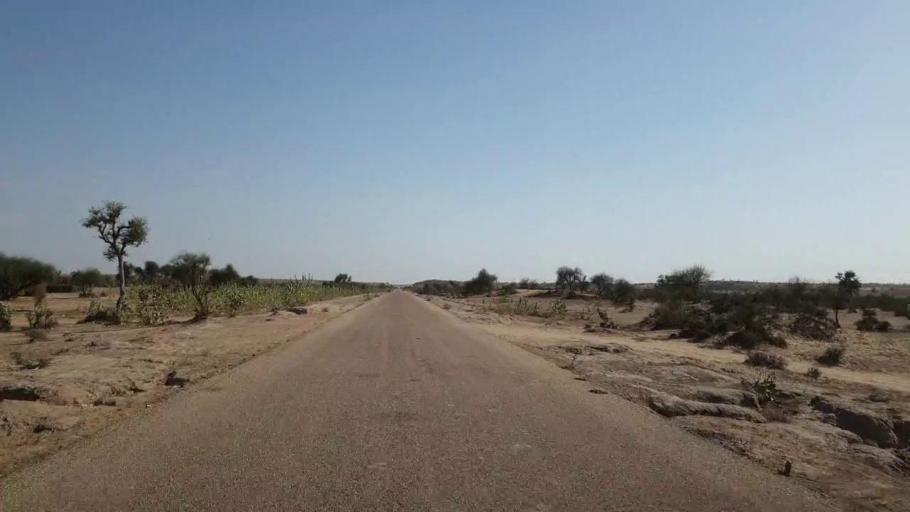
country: PK
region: Sindh
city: Nabisar
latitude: 25.0962
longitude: 70.0390
